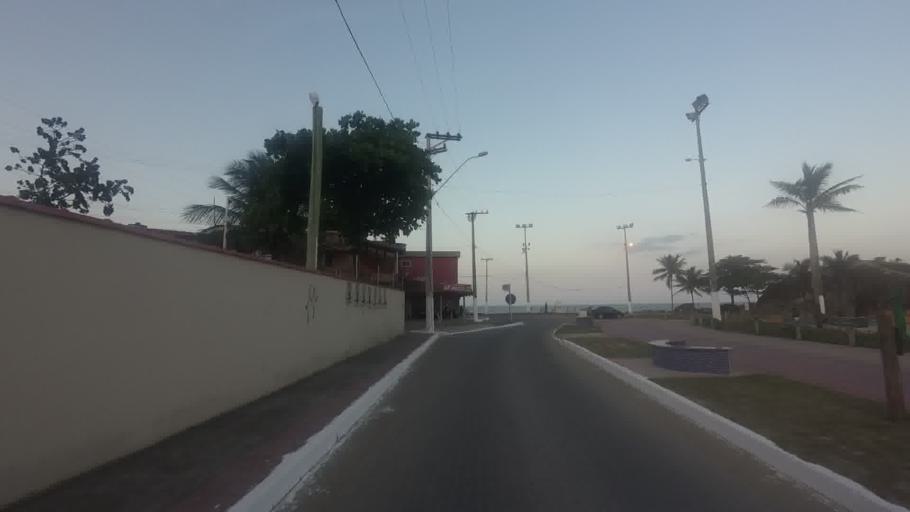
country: BR
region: Espirito Santo
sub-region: Piuma
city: Piuma
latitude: -20.9045
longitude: -40.7779
